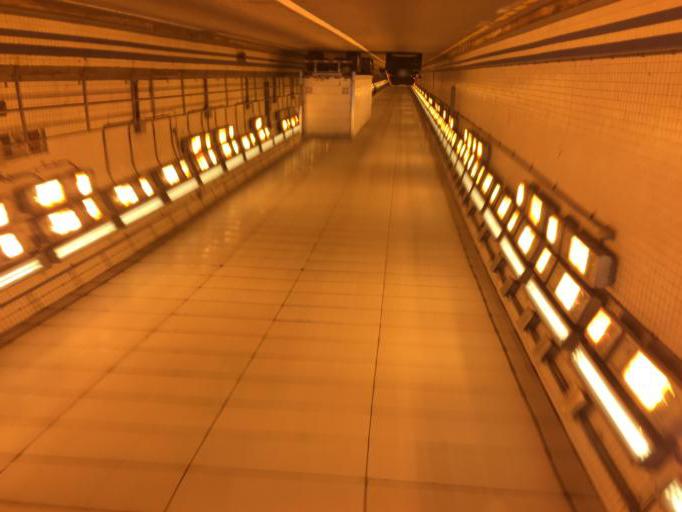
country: US
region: Virginia
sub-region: City of Hampton
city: East Hampton
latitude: 37.0006
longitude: -76.3184
